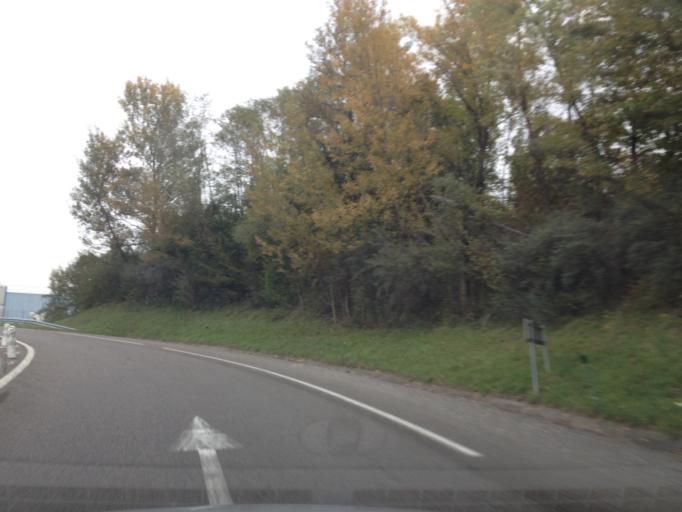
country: FR
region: Rhone-Alpes
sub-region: Departement de la Savoie
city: Gresy-sur-Aix
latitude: 45.7147
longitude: 5.9253
